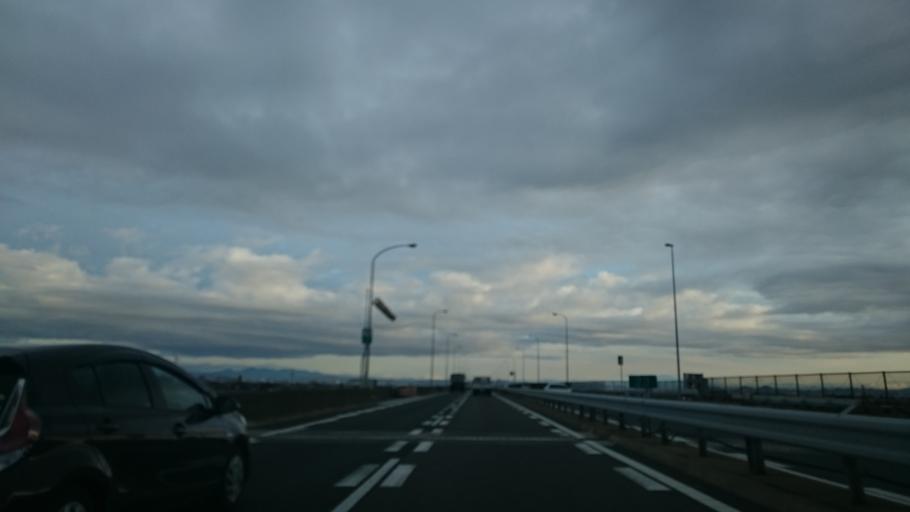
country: JP
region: Aichi
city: Inazawa
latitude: 35.2049
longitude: 136.8208
